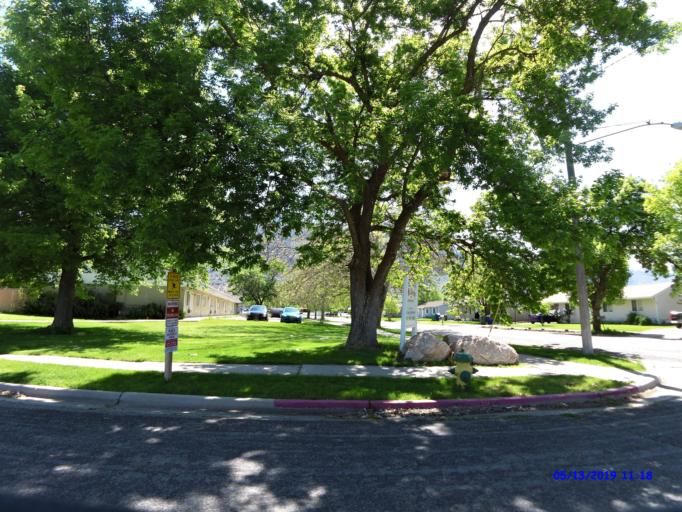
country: US
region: Utah
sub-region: Weber County
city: Harrisville
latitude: 41.2800
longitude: -111.9678
